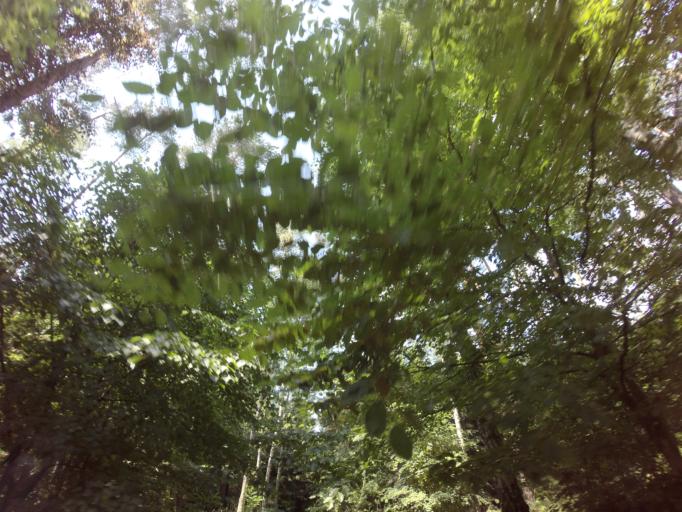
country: PL
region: West Pomeranian Voivodeship
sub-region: Powiat choszczenski
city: Bierzwnik
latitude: 53.0873
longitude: 15.6885
